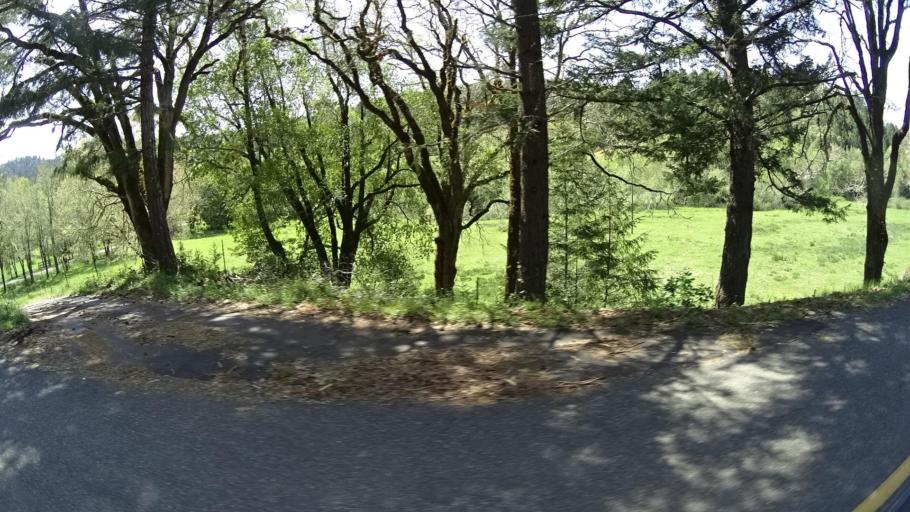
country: US
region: California
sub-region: Humboldt County
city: Redway
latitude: 40.3014
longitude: -123.6541
